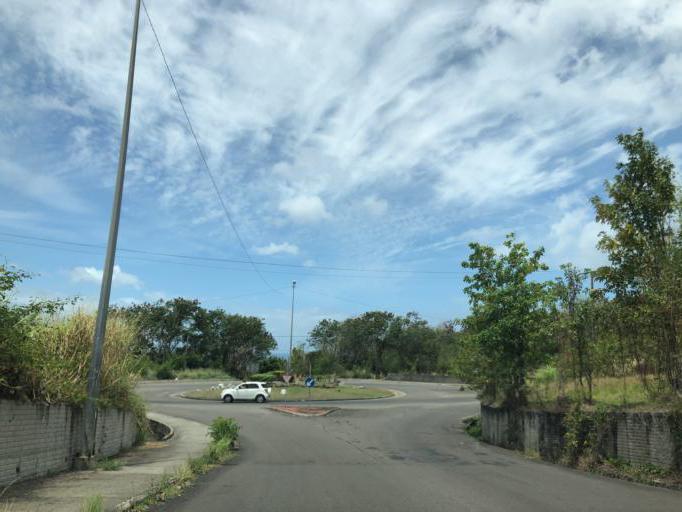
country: LC
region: Castries Quarter
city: Castries
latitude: 14.0032
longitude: -61.0113
